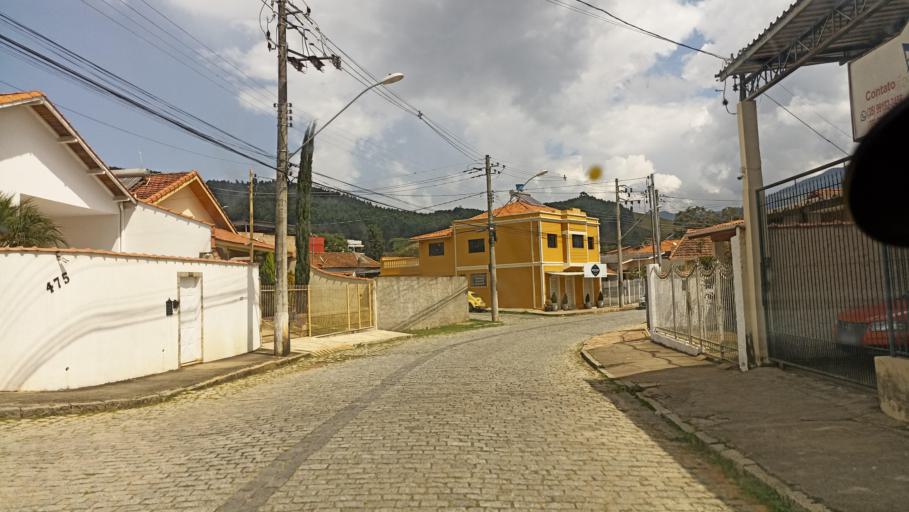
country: BR
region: Minas Gerais
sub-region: Passa Quatro
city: Passa Quatro
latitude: -22.3950
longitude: -44.9658
